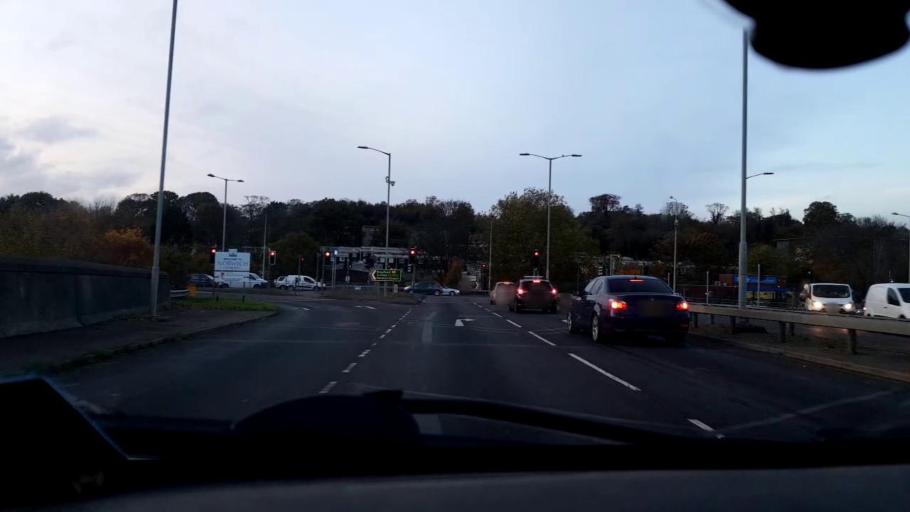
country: GB
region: England
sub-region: Norfolk
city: Thorpe Hamlet
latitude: 52.6114
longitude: 1.3074
